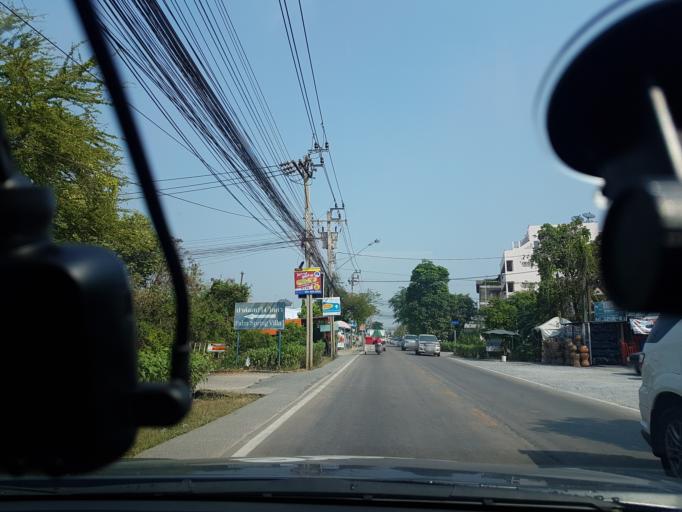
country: TH
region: Bangkok
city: Khan Na Yao
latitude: 13.8412
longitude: 100.7001
